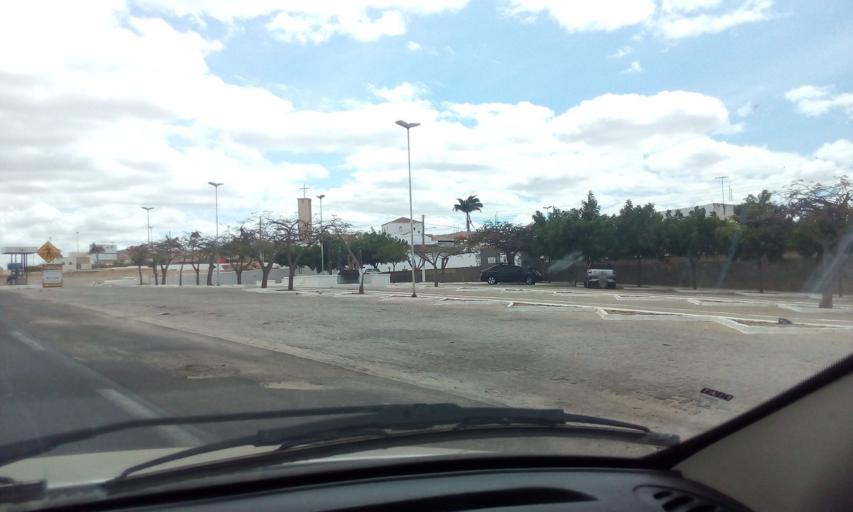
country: BR
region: Rio Grande do Norte
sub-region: Currais Novos
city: Currais Novos
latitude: -6.2581
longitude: -36.5054
